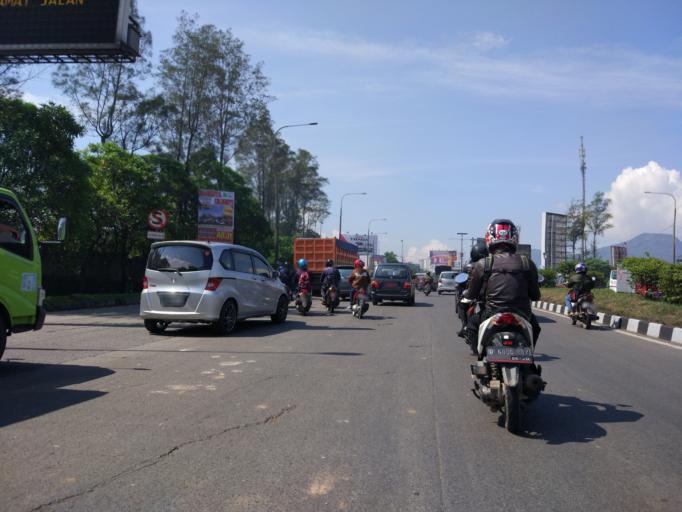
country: ID
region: West Java
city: Cileunyi
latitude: -6.9426
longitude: 107.7535
